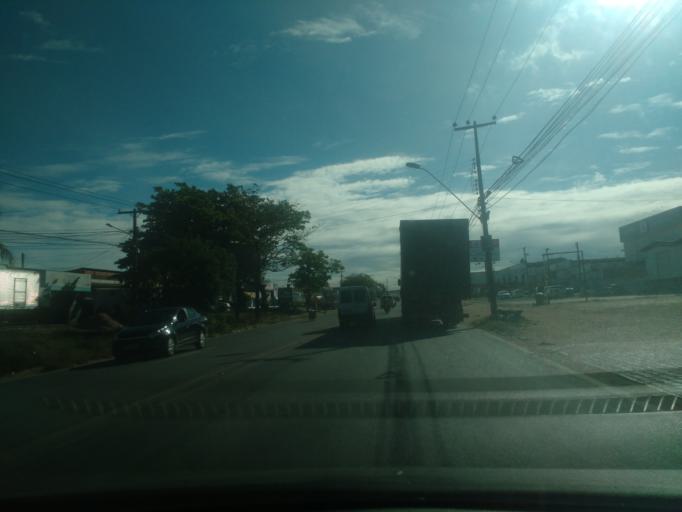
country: BR
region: Alagoas
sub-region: Satuba
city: Satuba
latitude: -9.5616
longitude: -35.7686
